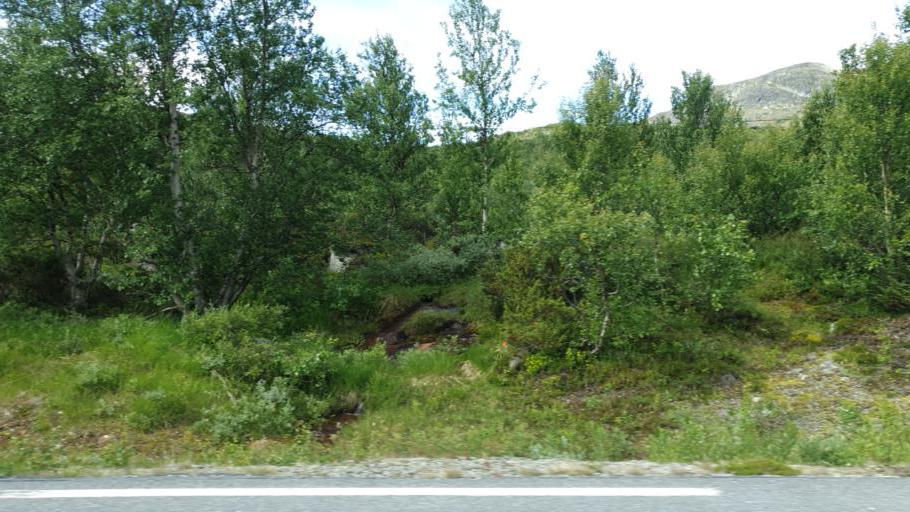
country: NO
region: Oppland
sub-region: Oystre Slidre
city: Heggenes
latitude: 61.5033
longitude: 8.8404
